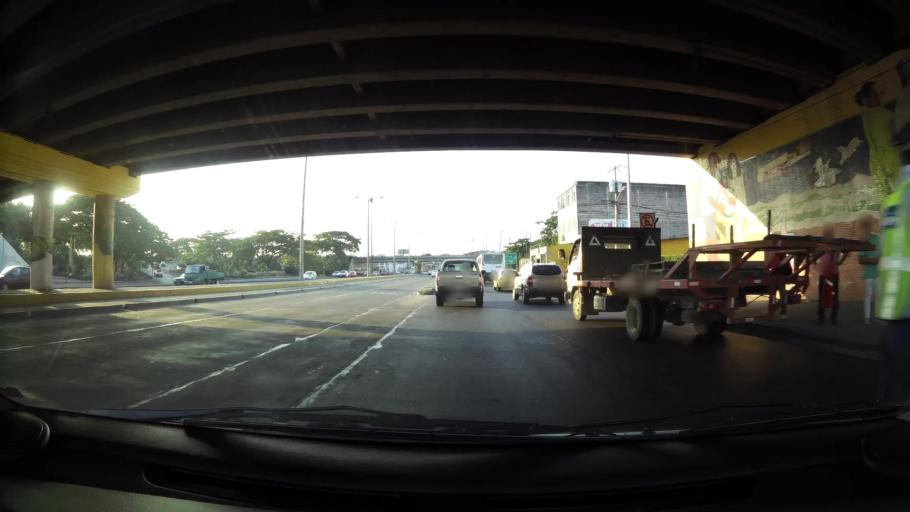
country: EC
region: Guayas
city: Guayaquil
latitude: -2.1415
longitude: -79.9341
